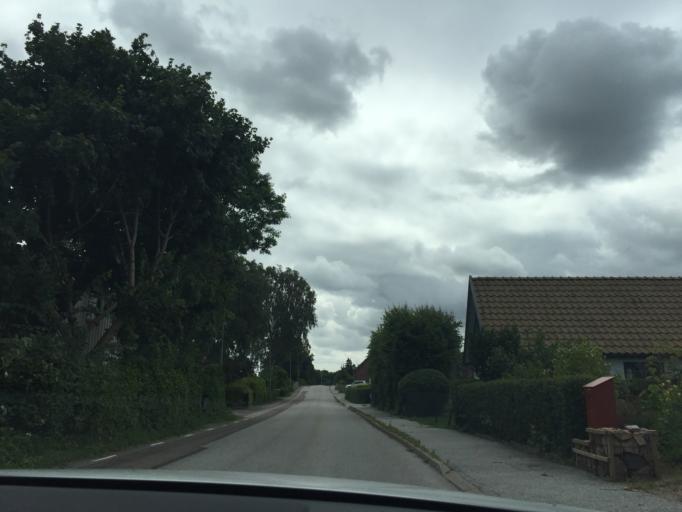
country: SE
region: Skane
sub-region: Sjobo Kommun
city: Blentarp
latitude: 55.5895
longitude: 13.5995
